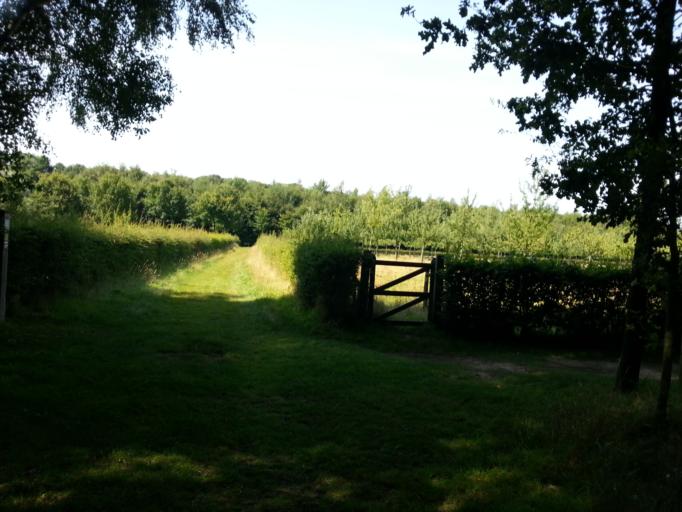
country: BE
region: Flanders
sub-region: Provincie West-Vlaanderen
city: Ieper
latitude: 50.8191
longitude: 2.9102
